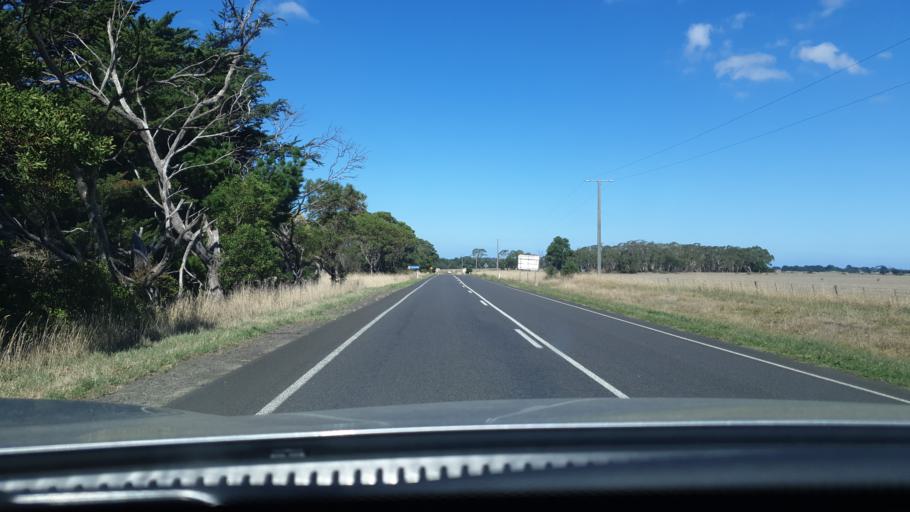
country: AU
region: Victoria
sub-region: Warrnambool
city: Warrnambool
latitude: -38.1800
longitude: 142.4237
